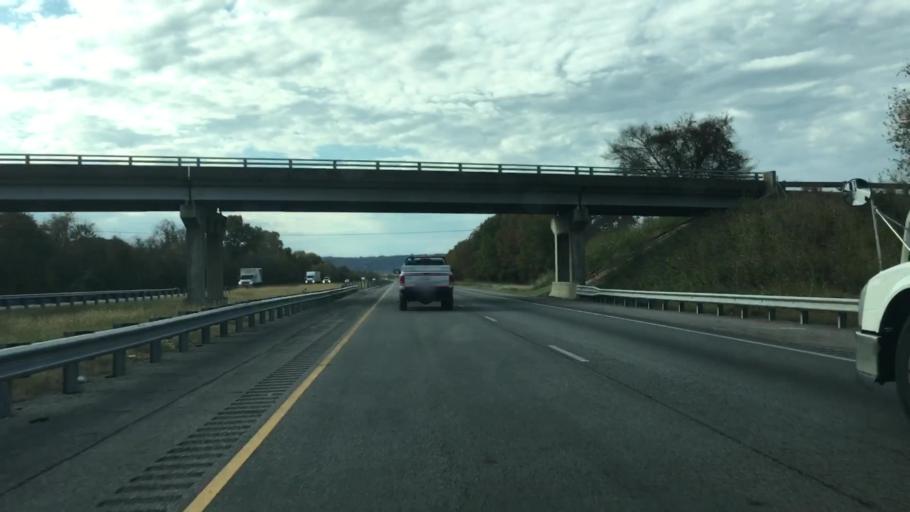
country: US
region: Arkansas
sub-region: Pope County
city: Atkins
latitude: 35.2477
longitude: -92.8718
